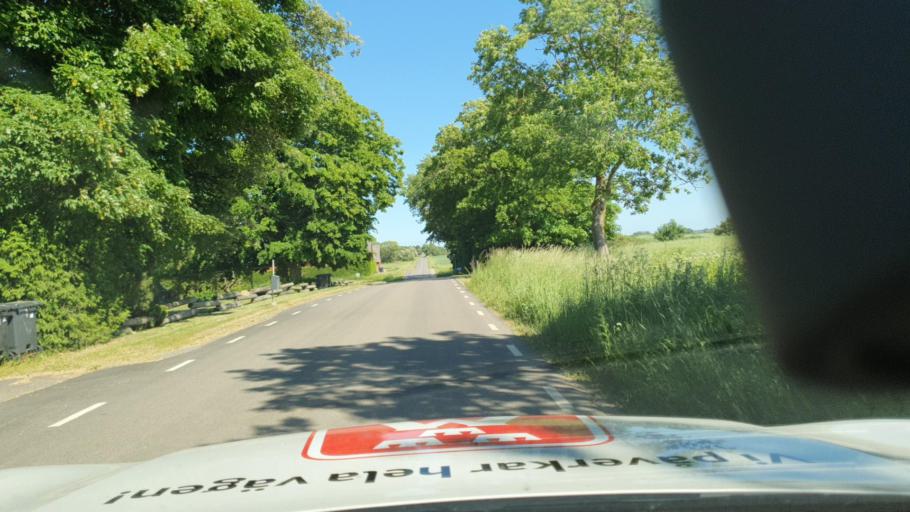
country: SE
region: Skane
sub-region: Sjobo Kommun
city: Sjoebo
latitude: 55.6561
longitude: 13.7185
